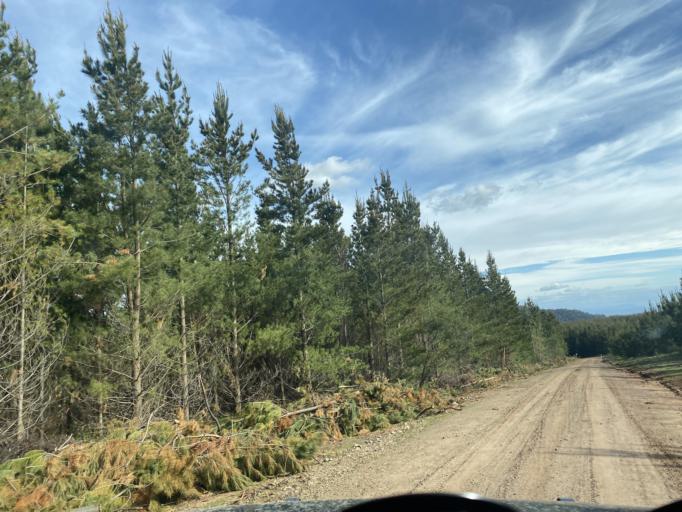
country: AU
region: Victoria
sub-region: Mansfield
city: Mansfield
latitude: -36.8337
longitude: 146.1793
